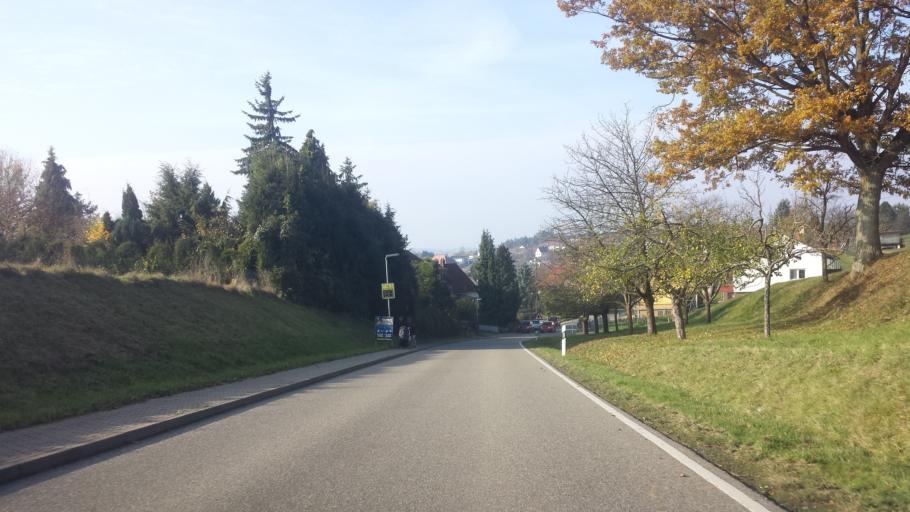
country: DE
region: Baden-Wuerttemberg
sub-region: Karlsruhe Region
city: Epfenbach
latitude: 49.3353
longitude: 8.9173
